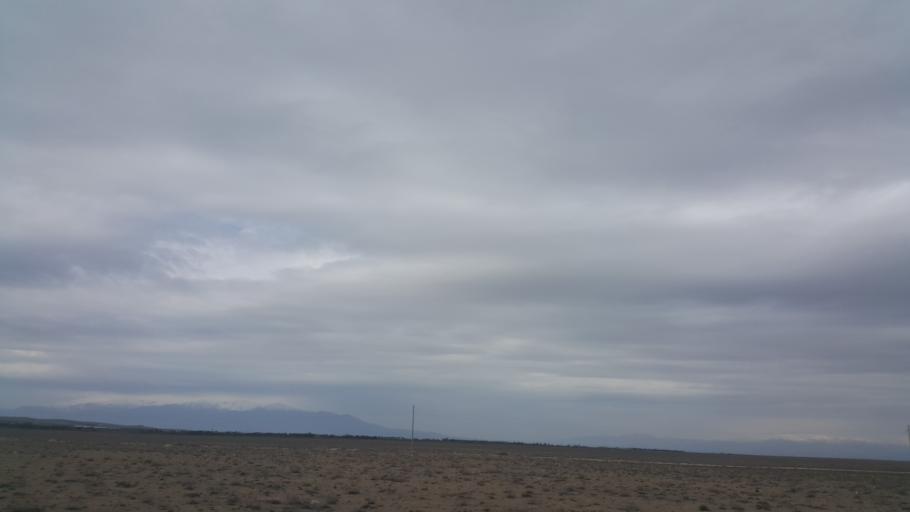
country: TR
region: Nigde
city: Altunhisar
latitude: 37.7772
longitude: 34.2396
